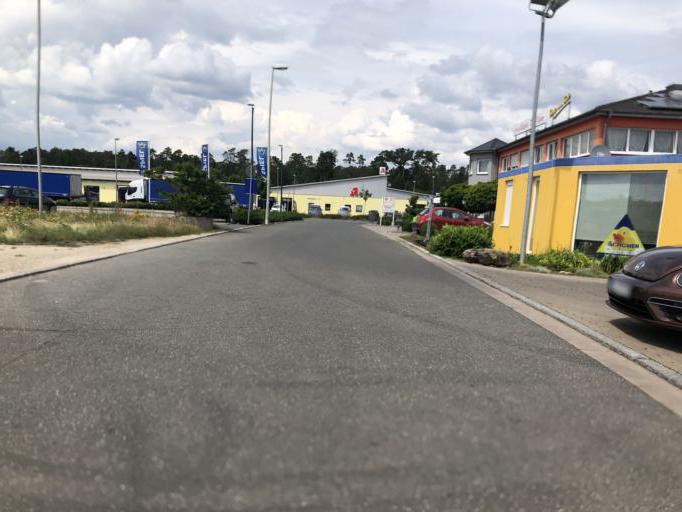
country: DE
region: Bavaria
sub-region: Regierungsbezirk Mittelfranken
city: Hessdorf
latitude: 49.6265
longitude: 10.9239
